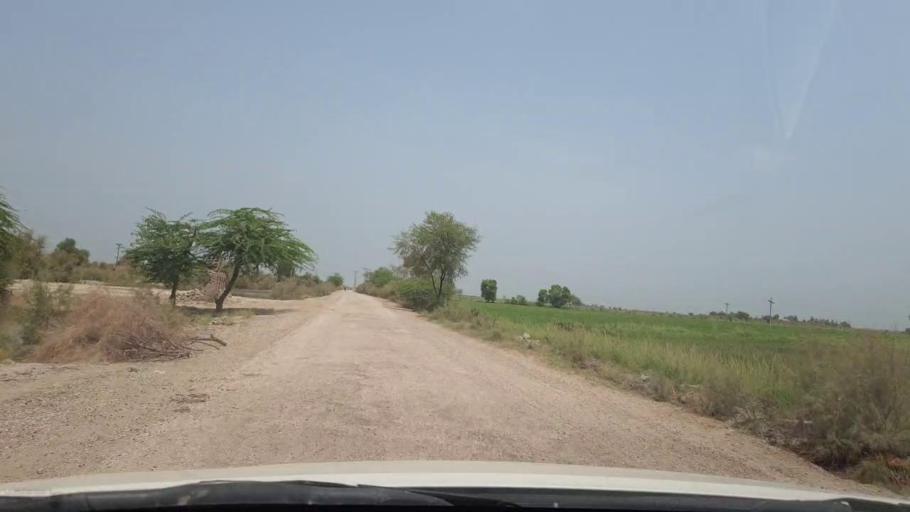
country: PK
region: Sindh
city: Rustam jo Goth
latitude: 28.0455
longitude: 68.8151
